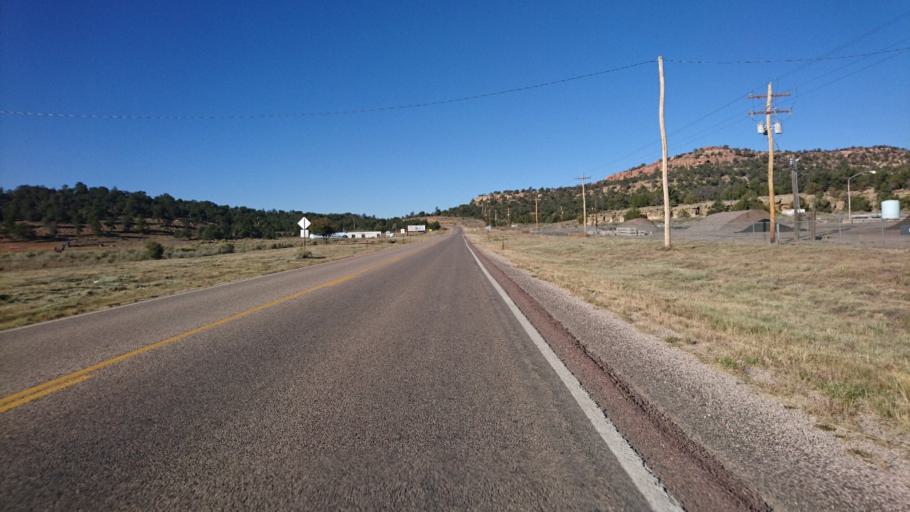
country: US
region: New Mexico
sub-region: McKinley County
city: Black Rock
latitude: 35.1325
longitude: -108.5183
